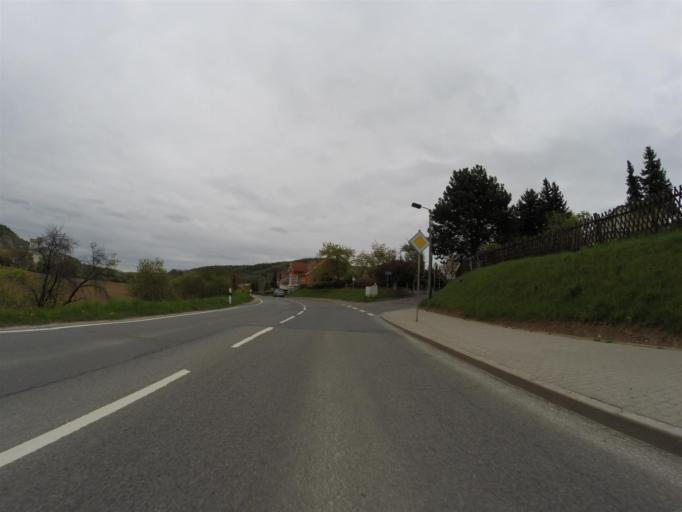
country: DE
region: Thuringia
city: Wichmar
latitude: 51.0094
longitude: 11.6859
